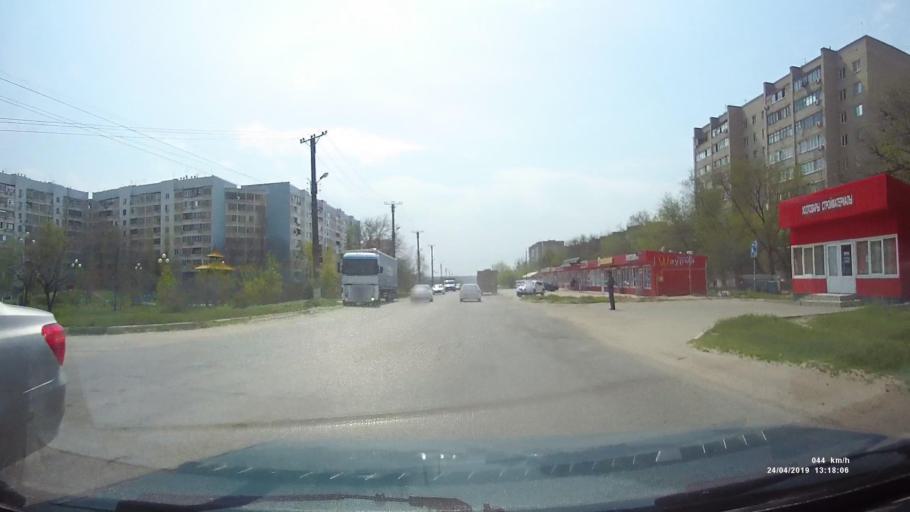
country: RU
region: Kalmykiya
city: Elista
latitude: 46.3038
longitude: 44.2962
